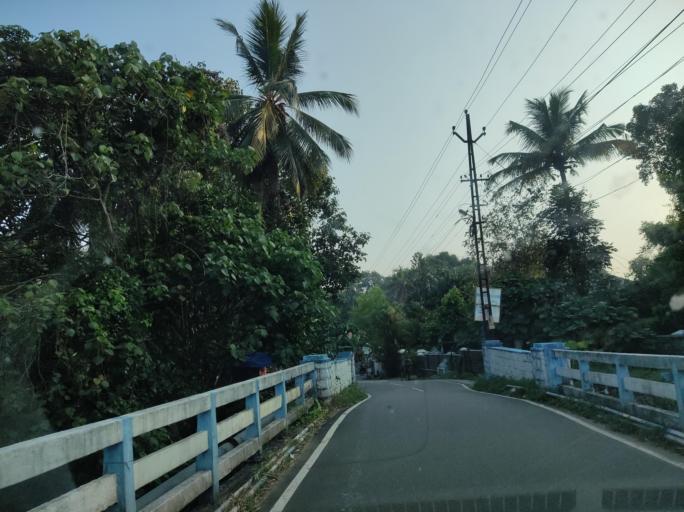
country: IN
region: Kerala
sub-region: Pattanamtitta
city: Tiruvalla
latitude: 9.3668
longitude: 76.5646
